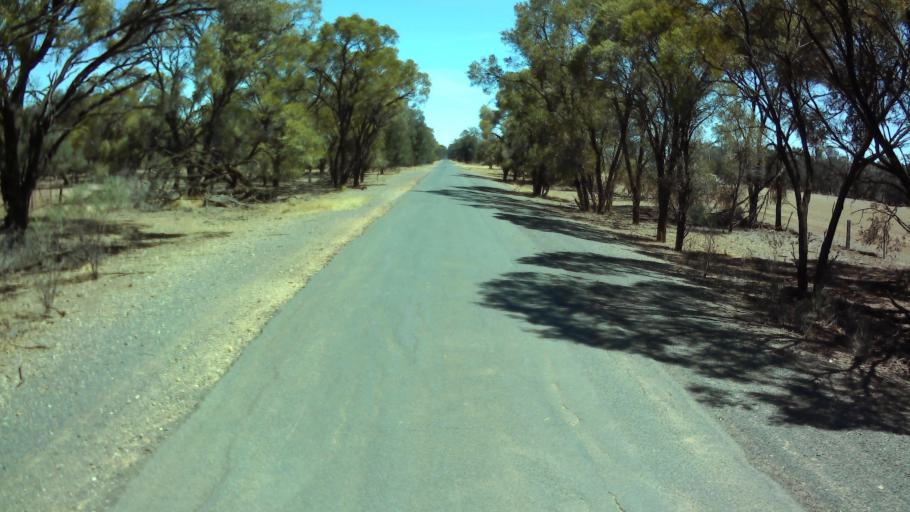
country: AU
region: New South Wales
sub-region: Weddin
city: Grenfell
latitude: -33.8716
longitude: 147.6918
